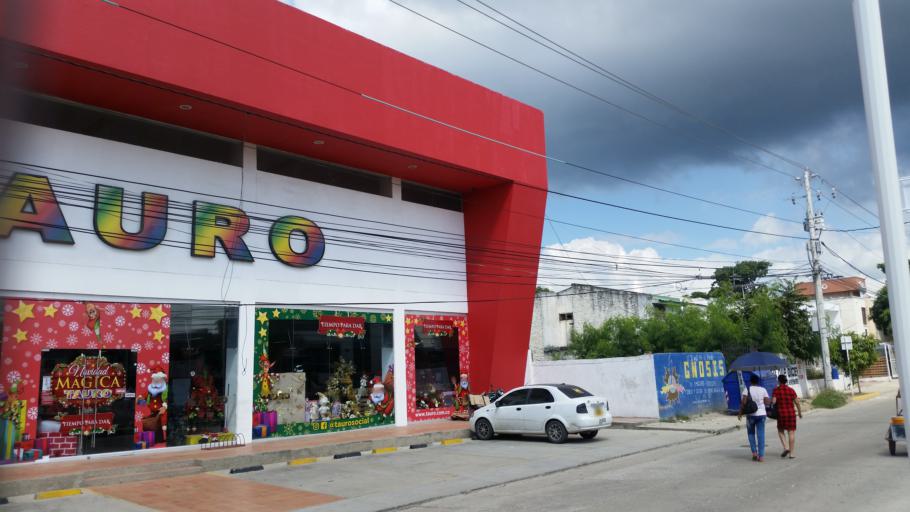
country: CO
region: Magdalena
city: Santa Marta
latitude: 11.2412
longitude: -74.1896
